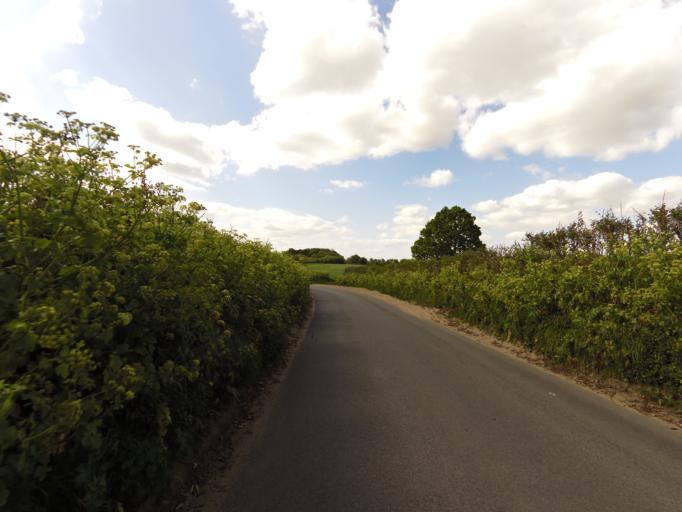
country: GB
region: England
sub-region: Suffolk
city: Kessingland
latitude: 52.4406
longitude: 1.6629
